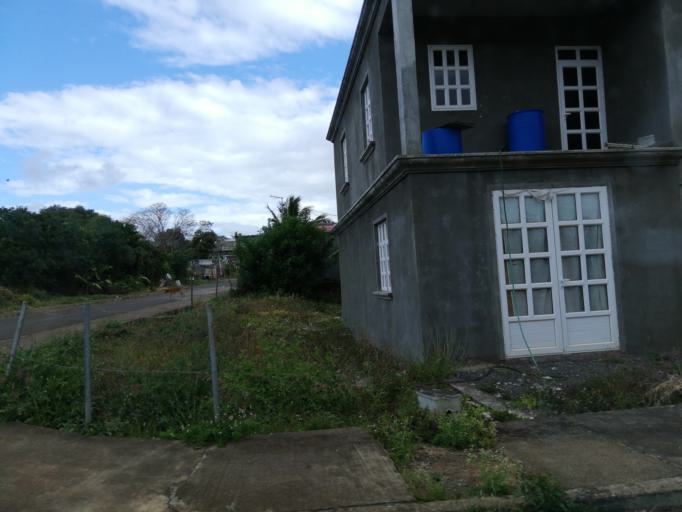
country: MU
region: Black River
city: Petite Riviere
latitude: -20.2105
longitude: 57.4644
